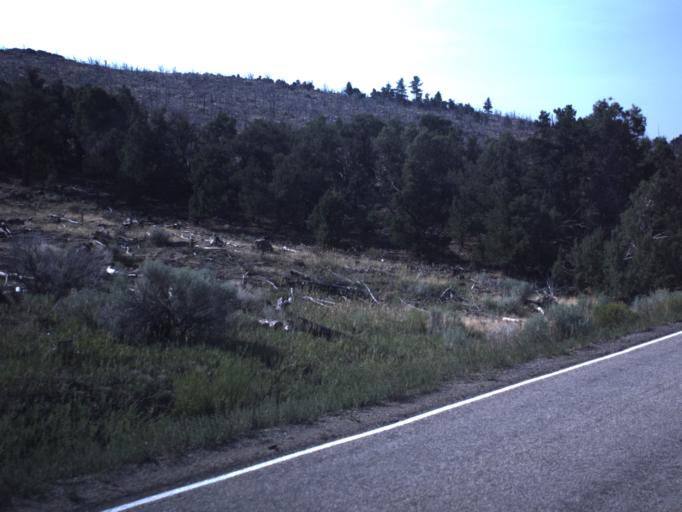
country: US
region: Utah
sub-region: Daggett County
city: Manila
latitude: 40.9265
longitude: -109.4158
